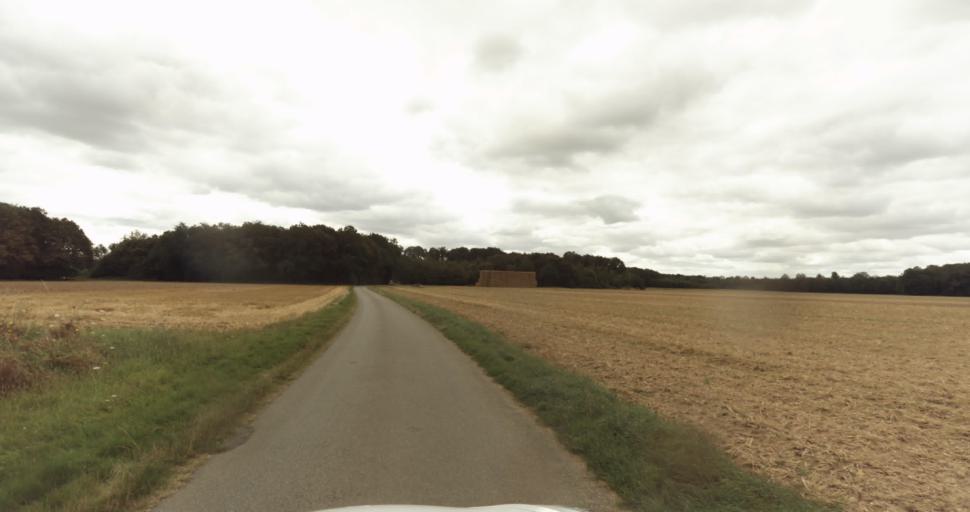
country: FR
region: Haute-Normandie
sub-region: Departement de l'Eure
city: La Madeleine-de-Nonancourt
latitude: 48.8177
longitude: 1.2065
